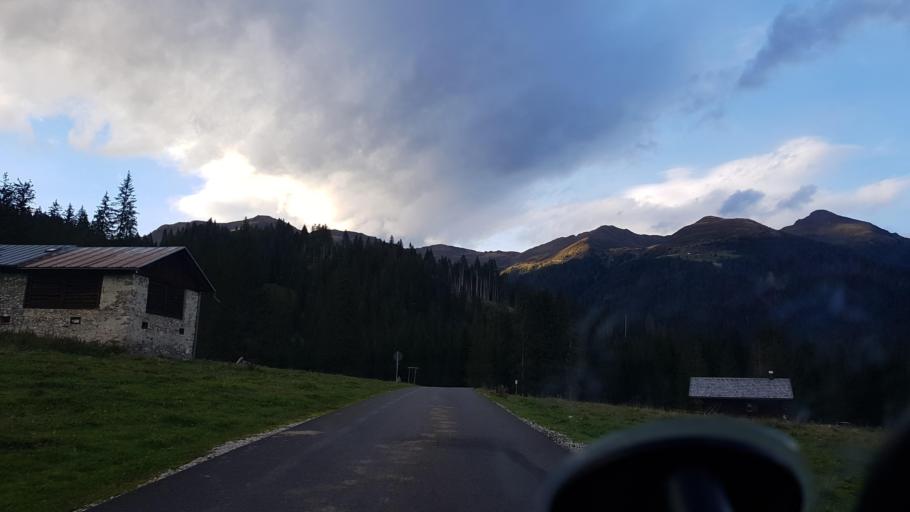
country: IT
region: Veneto
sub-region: Provincia di Belluno
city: San Pietro di Cadore
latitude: 46.6138
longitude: 12.6242
